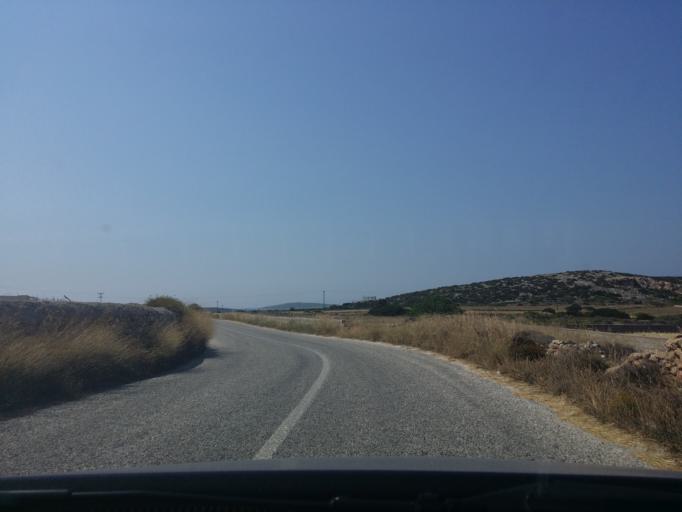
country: GR
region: South Aegean
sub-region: Nomos Kykladon
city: Antiparos
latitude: 37.0180
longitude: 25.1107
